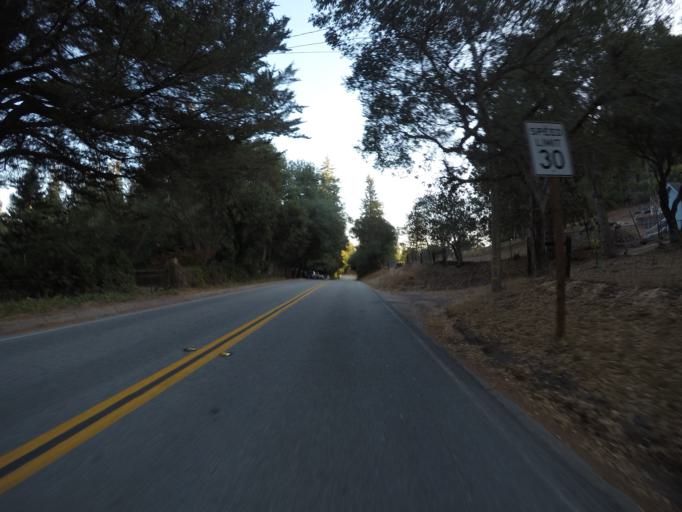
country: US
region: California
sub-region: Santa Cruz County
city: Pasatiempo
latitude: 37.0235
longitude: -122.0287
